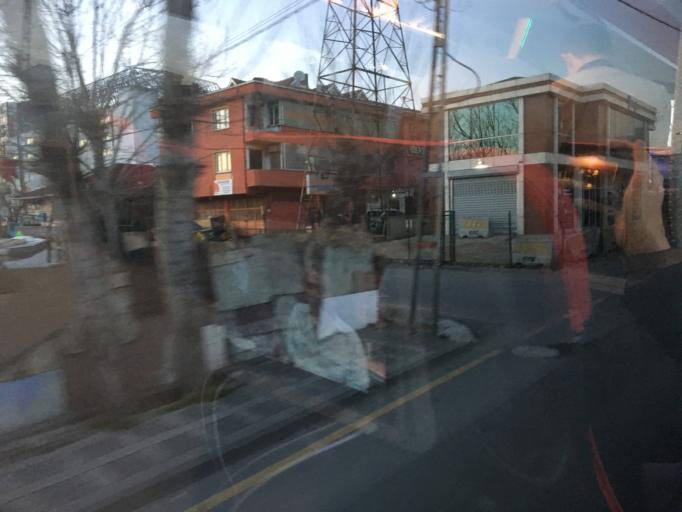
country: TR
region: Istanbul
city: Umraniye
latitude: 40.9978
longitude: 29.1487
